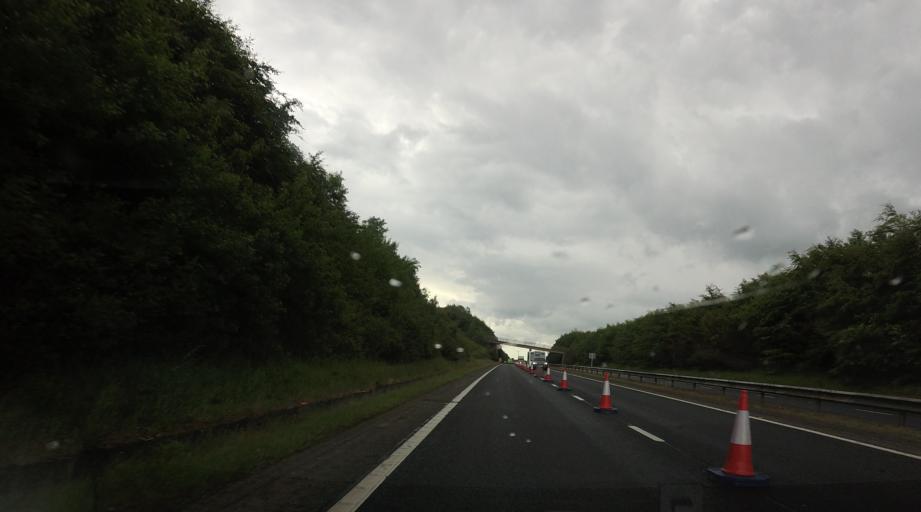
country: GB
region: Scotland
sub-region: Fife
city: Lochgelly
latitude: 56.1177
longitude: -3.3076
